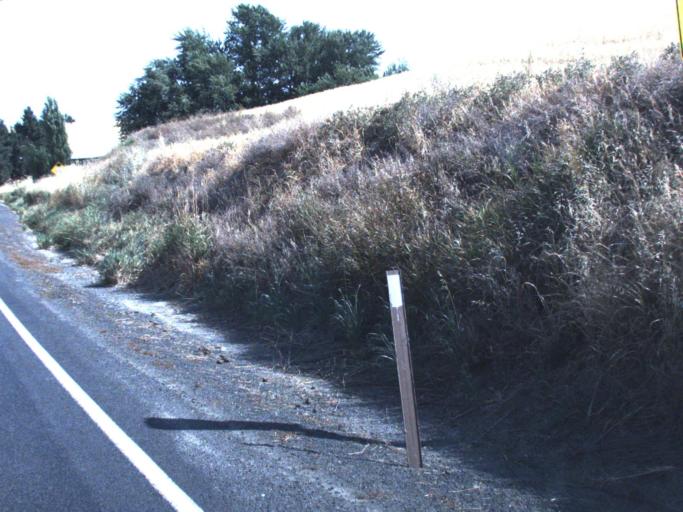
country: US
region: Idaho
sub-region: Benewah County
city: Plummer
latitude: 47.2159
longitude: -117.0794
